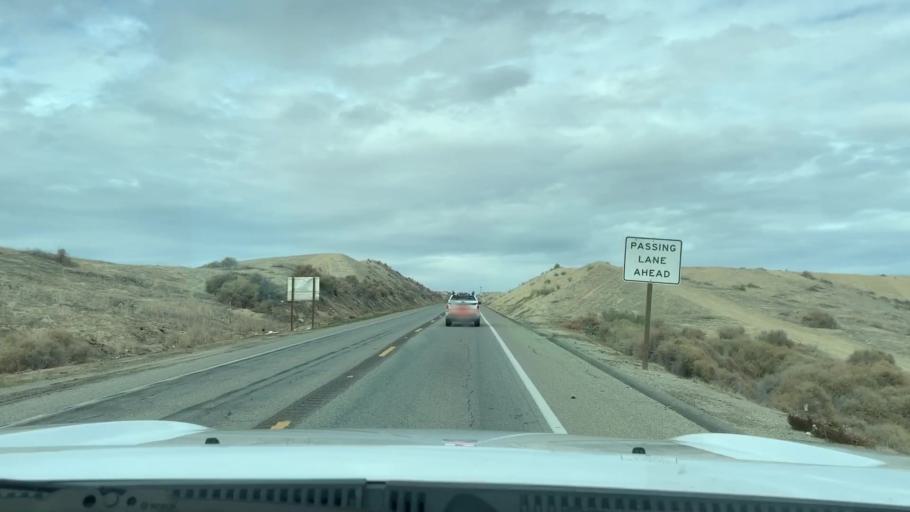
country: US
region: California
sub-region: Kern County
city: Maricopa
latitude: 35.0972
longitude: -119.4120
